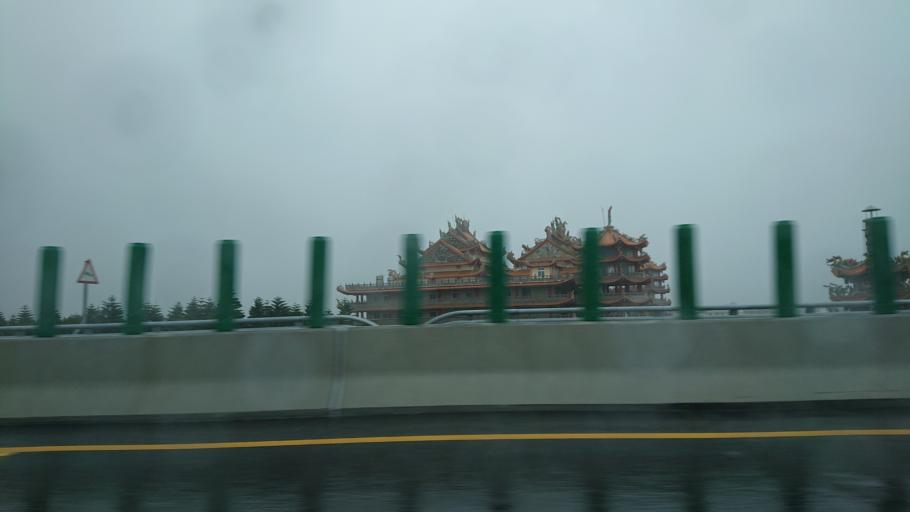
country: TW
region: Taiwan
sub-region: Changhua
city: Chang-hua
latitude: 23.9300
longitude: 120.3155
